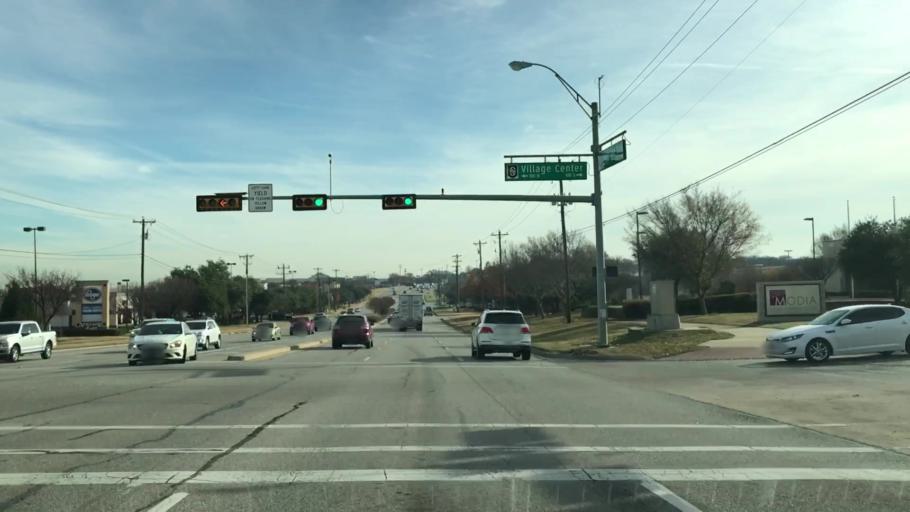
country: US
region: Texas
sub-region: Tarrant County
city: Southlake
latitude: 32.9409
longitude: -97.1230
